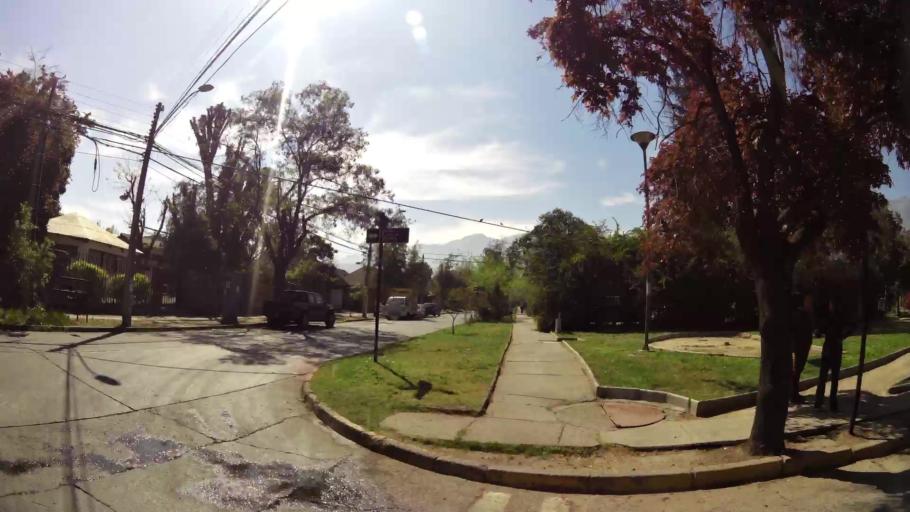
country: CL
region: Santiago Metropolitan
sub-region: Provincia de Santiago
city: Villa Presidente Frei, Nunoa, Santiago, Chile
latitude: -33.4462
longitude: -70.5407
